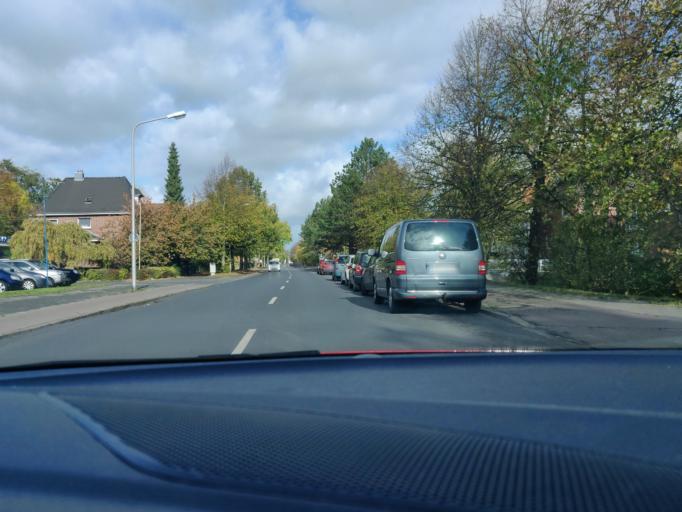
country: DE
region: Lower Saxony
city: Cuxhaven
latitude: 53.8500
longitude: 8.6883
